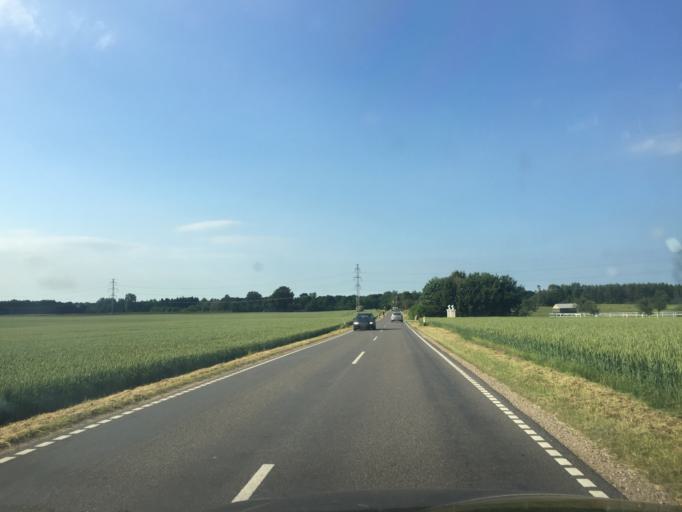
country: DK
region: Capital Region
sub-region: Hoje-Taastrup Kommune
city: Taastrup
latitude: 55.6972
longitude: 12.2546
